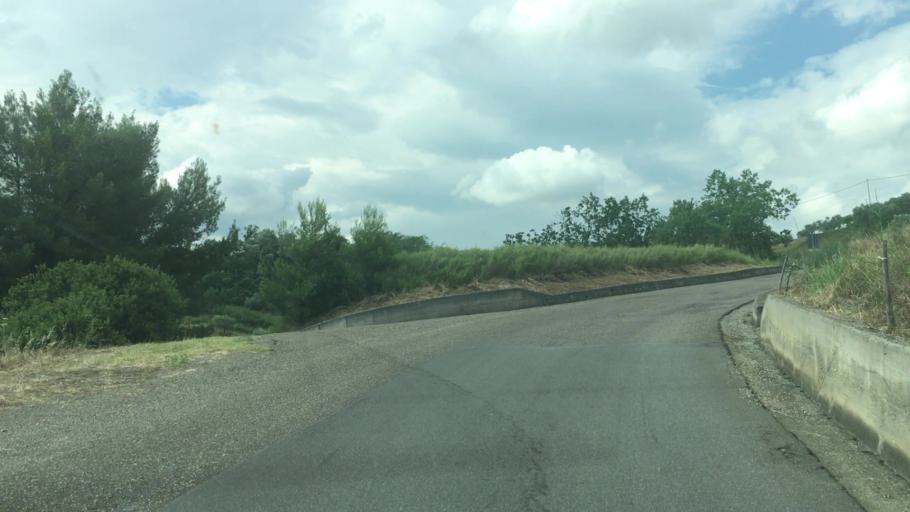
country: IT
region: Basilicate
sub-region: Provincia di Matera
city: San Mauro Forte
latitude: 40.4827
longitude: 16.2683
